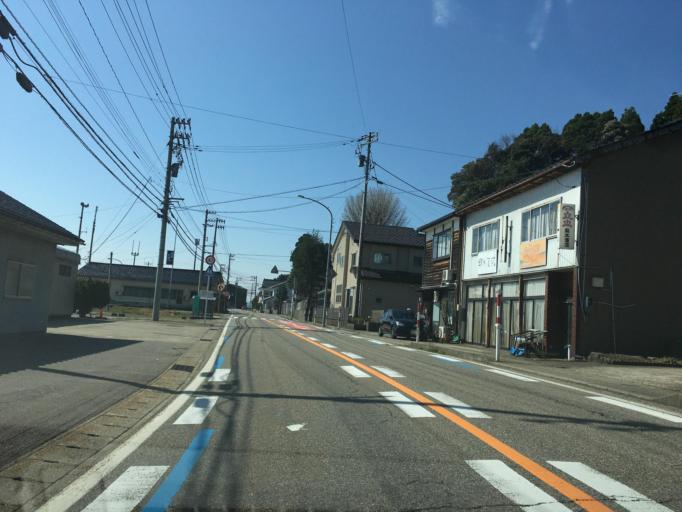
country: JP
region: Toyama
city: Himi
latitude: 36.8966
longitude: 137.0069
